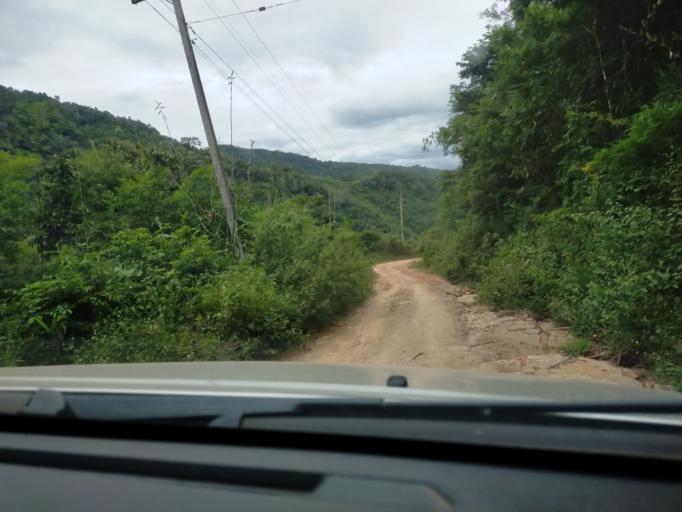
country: TH
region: Nan
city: Chaloem Phra Kiat
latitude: 19.8003
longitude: 101.3629
